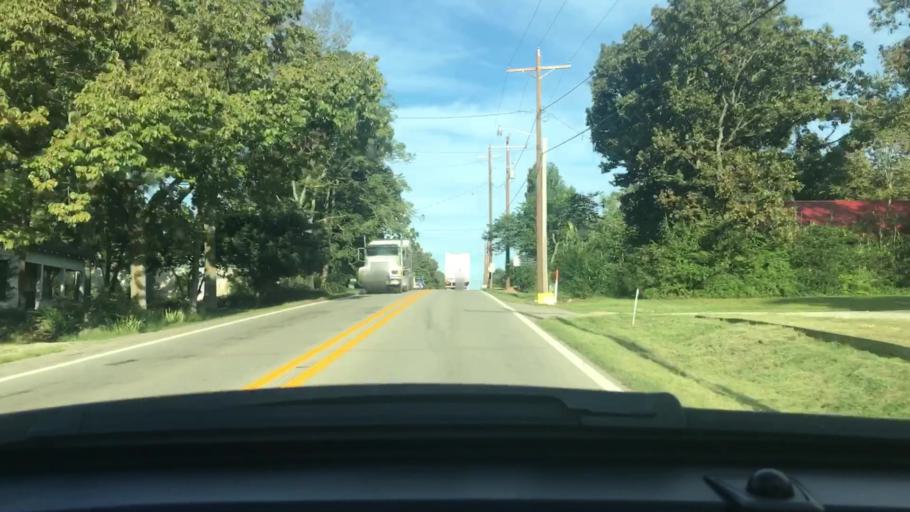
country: US
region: Arkansas
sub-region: Randolph County
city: Pocahontas
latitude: 36.2039
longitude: -91.1868
